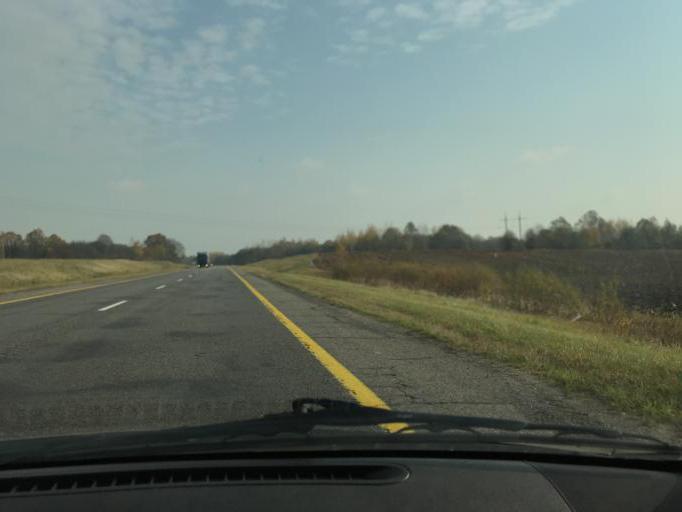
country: BY
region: Vitebsk
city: Chashniki
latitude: 54.9953
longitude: 28.9395
